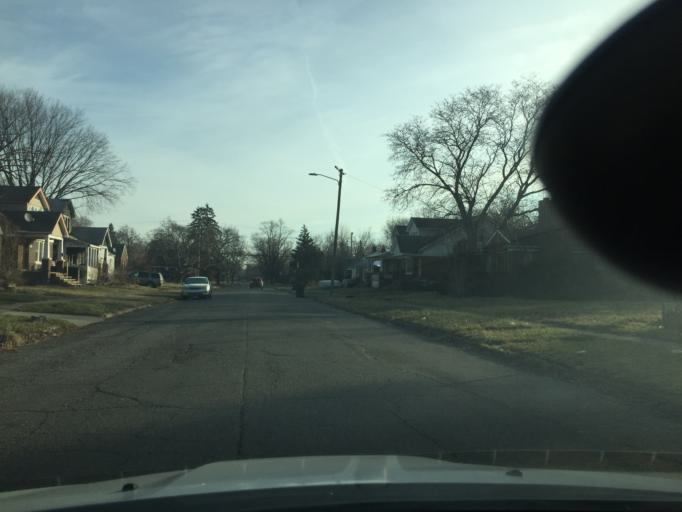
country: US
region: Michigan
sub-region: Macomb County
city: Eastpointe
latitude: 42.4393
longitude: -82.9702
